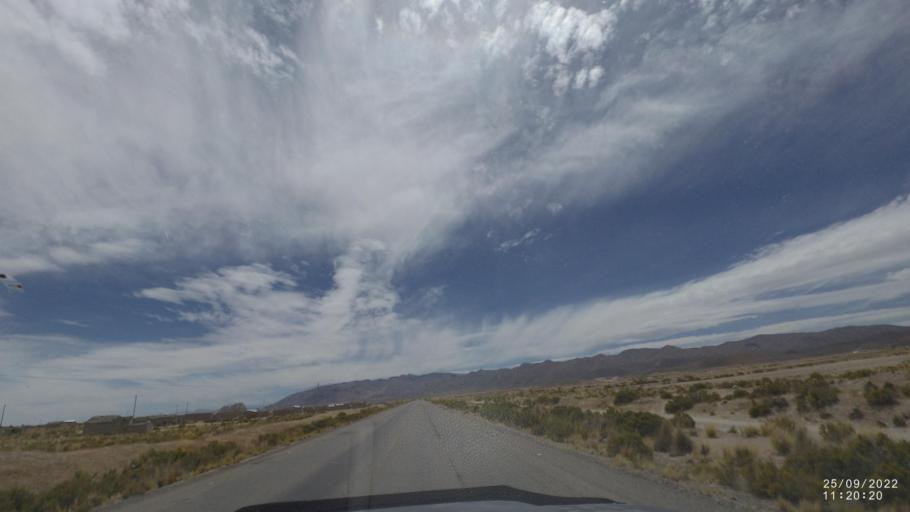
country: BO
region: Oruro
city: Challapata
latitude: -19.1607
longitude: -66.7767
